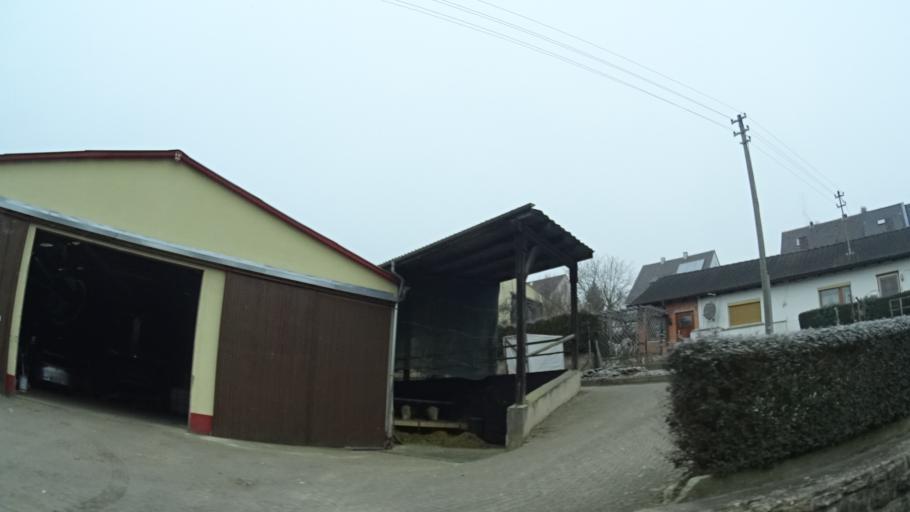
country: DE
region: Bavaria
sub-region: Regierungsbezirk Unterfranken
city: Burgpreppach
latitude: 50.1411
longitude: 10.6484
